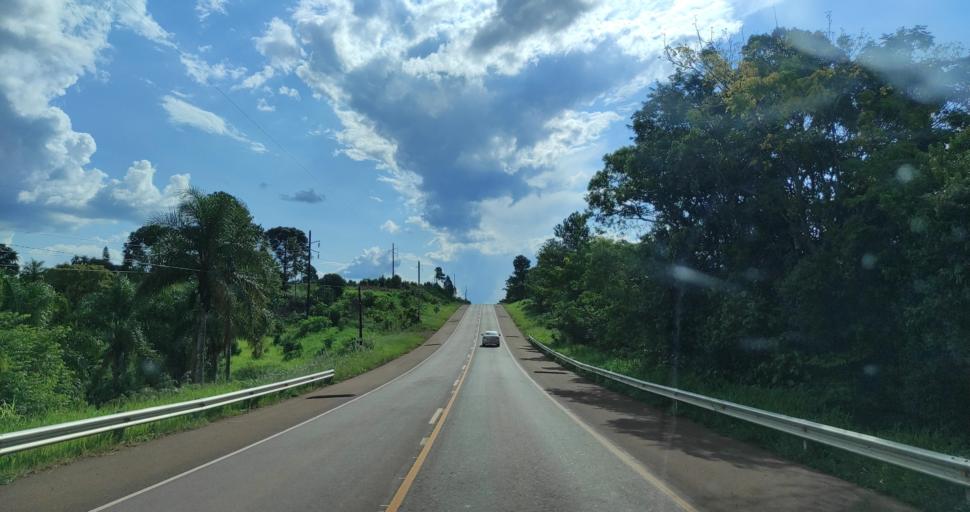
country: AR
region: Misiones
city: Bernardo de Irigoyen
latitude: -26.2941
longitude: -53.7757
